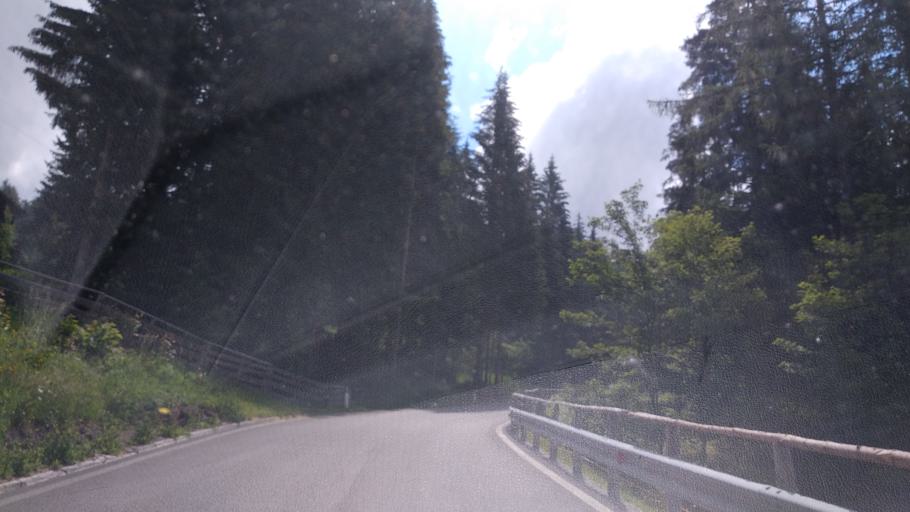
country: IT
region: Trentino-Alto Adige
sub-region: Bolzano
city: Avelengo
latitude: 46.6585
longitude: 11.2272
